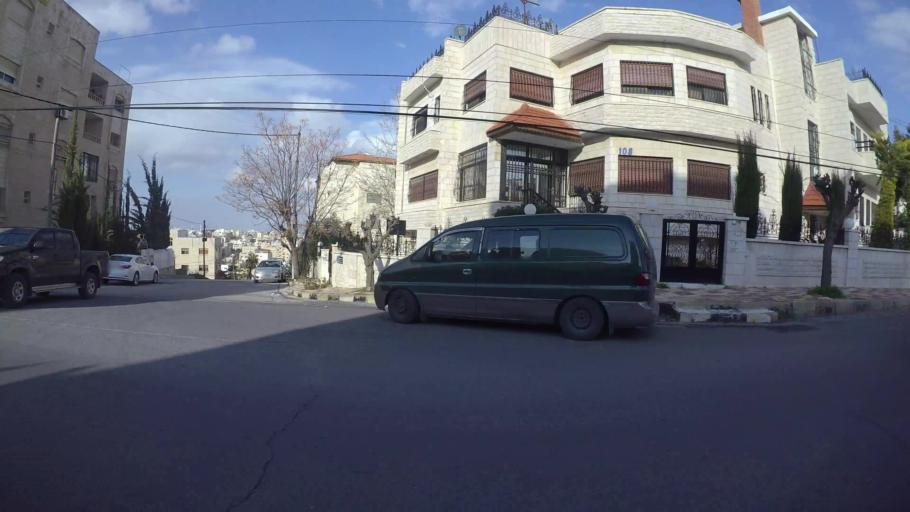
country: JO
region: Amman
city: Al Jubayhah
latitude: 32.0127
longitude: 35.8620
